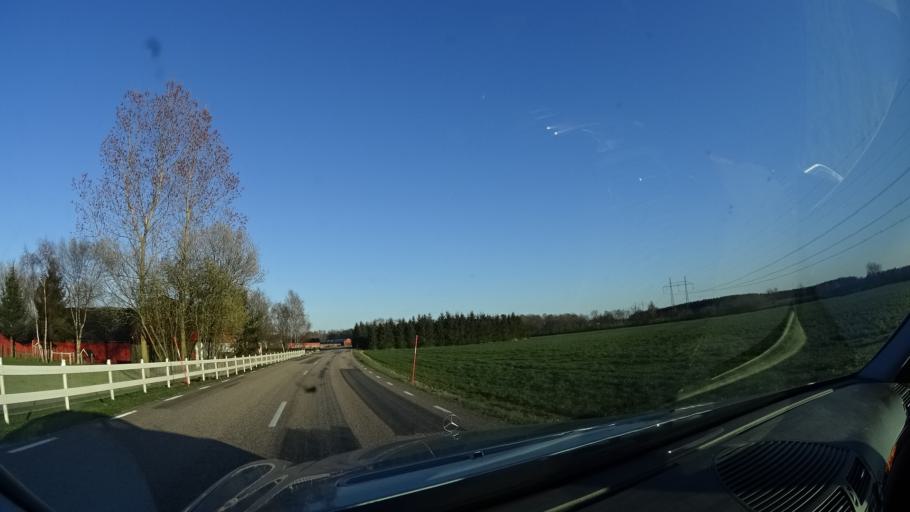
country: SE
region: Skane
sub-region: Bjuvs Kommun
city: Billesholm
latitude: 56.0395
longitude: 13.0183
